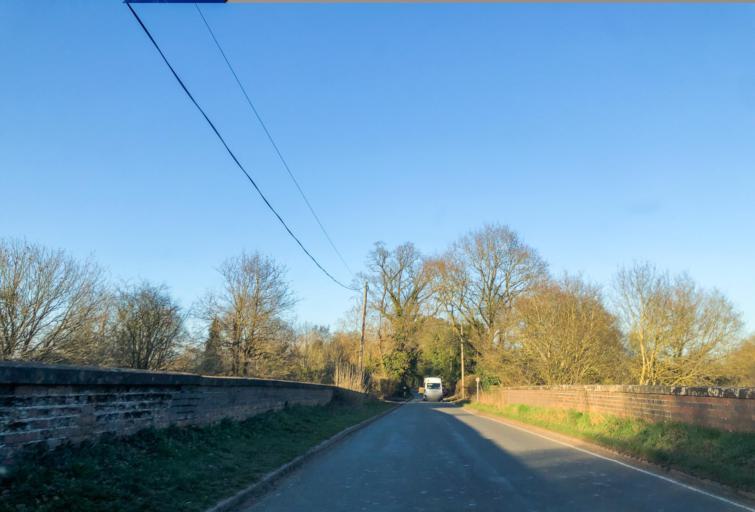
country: GB
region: England
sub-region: Warwickshire
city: Wroxall
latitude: 52.2972
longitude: -1.6583
